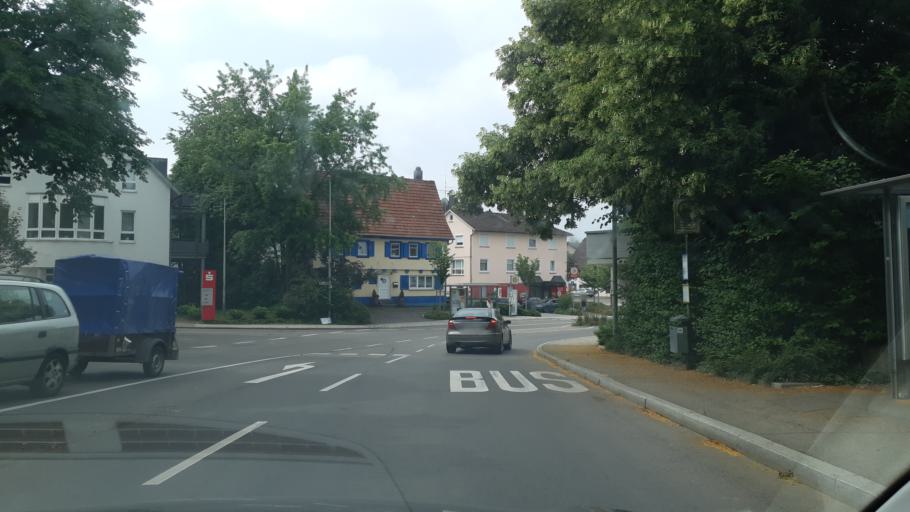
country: DE
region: Baden-Wuerttemberg
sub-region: Regierungsbezirk Stuttgart
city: Boll
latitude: 48.6679
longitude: 9.6159
